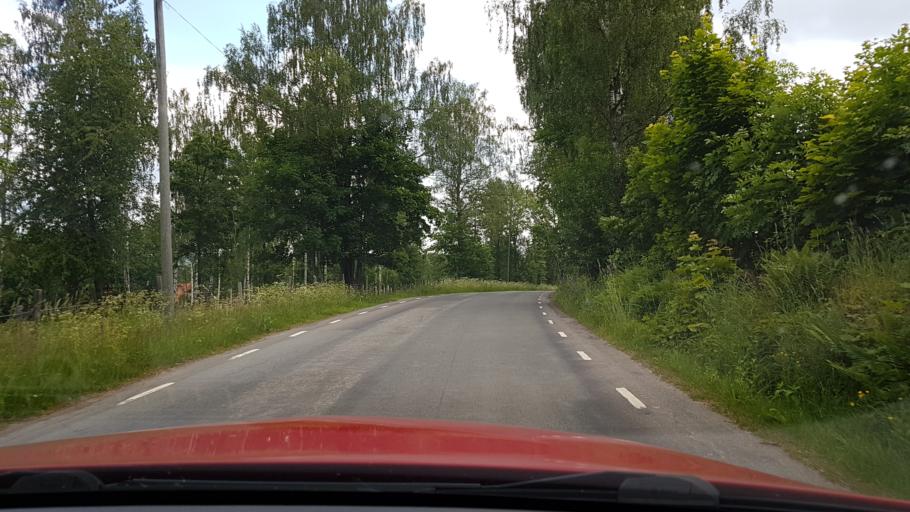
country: SE
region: Vaestra Goetaland
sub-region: Hjo Kommun
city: Hjo
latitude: 58.3113
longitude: 14.1807
